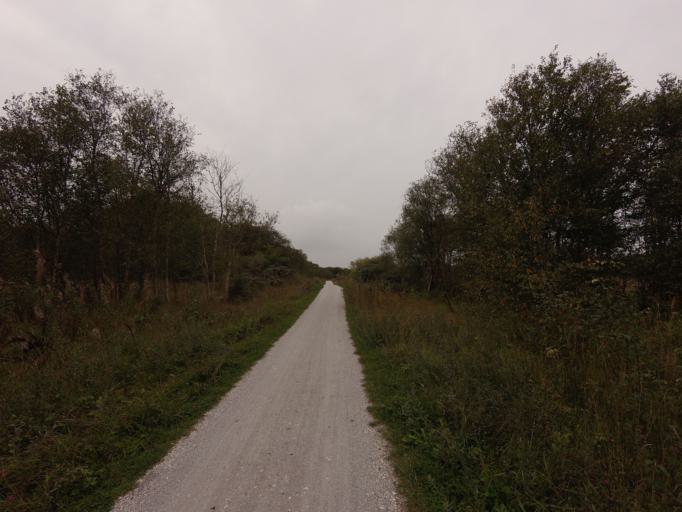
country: NL
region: Friesland
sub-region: Gemeente Schiermonnikoog
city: Schiermonnikoog
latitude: 53.4910
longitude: 6.1998
